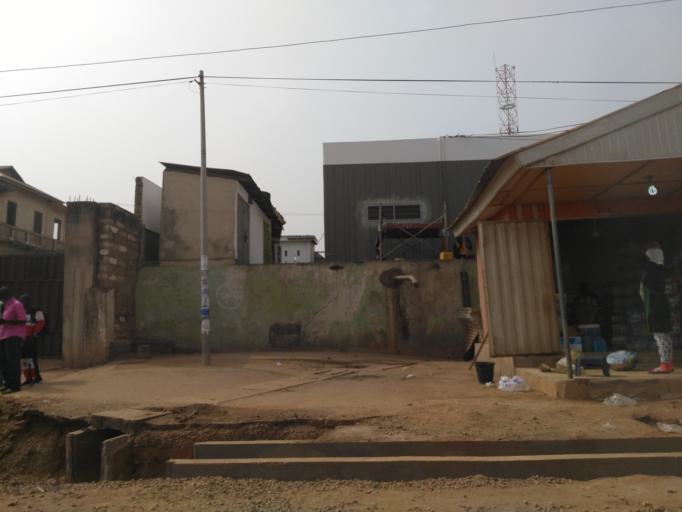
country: GH
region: Ashanti
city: Kumasi
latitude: 6.7090
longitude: -1.6264
